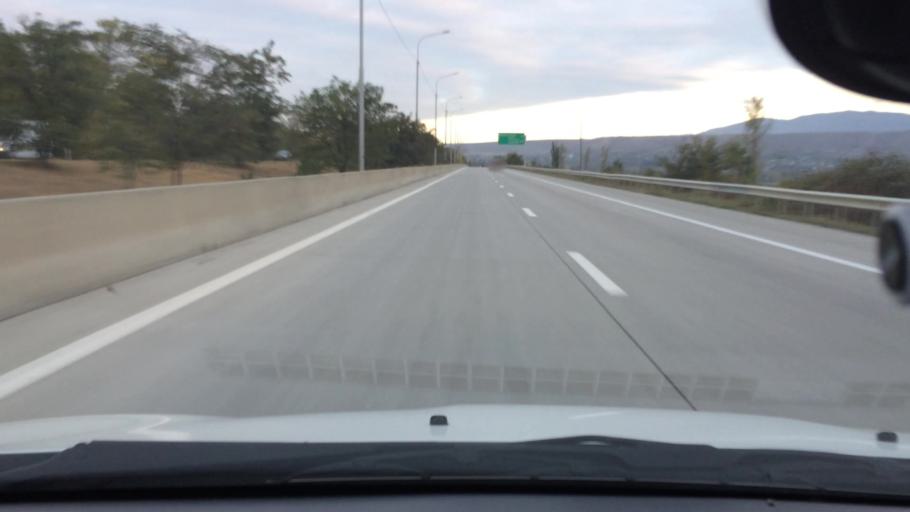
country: GE
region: Shida Kartli
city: Kaspi
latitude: 41.9509
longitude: 44.4983
